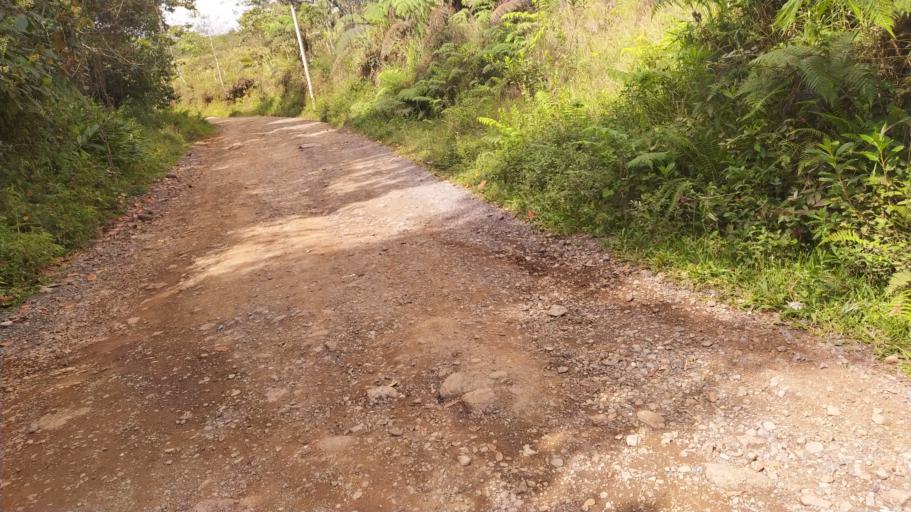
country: CO
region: Valle del Cauca
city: Cali
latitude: 3.4323
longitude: -76.6146
